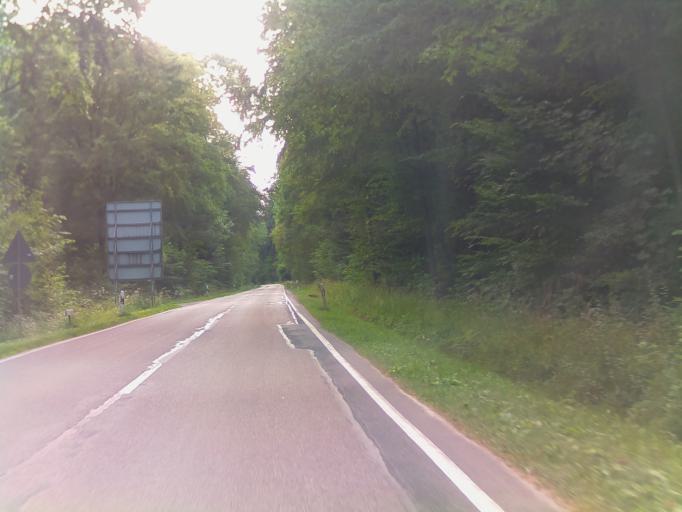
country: DE
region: Baden-Wuerttemberg
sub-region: Regierungsbezirk Stuttgart
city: Buch am Ahorn
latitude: 49.5389
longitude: 9.5800
